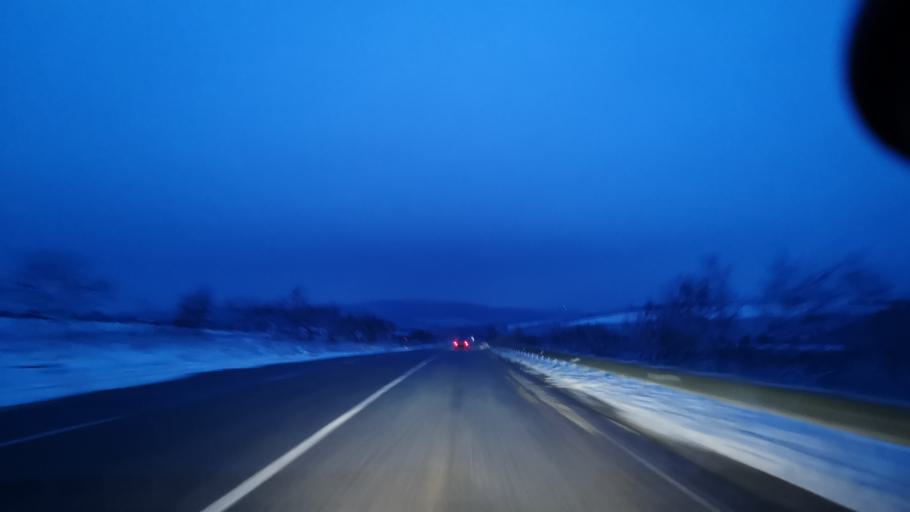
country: MD
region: Orhei
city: Orhei
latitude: 47.5312
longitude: 28.7948
